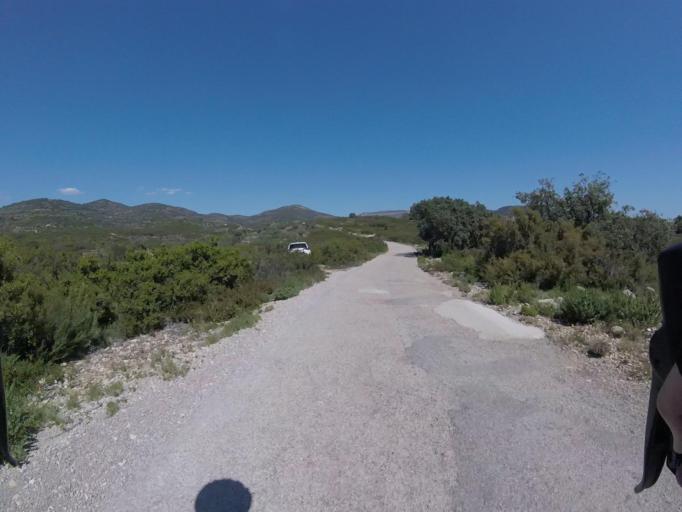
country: ES
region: Valencia
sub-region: Provincia de Castello
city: Sierra-Engarceran
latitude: 40.2354
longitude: -0.0263
